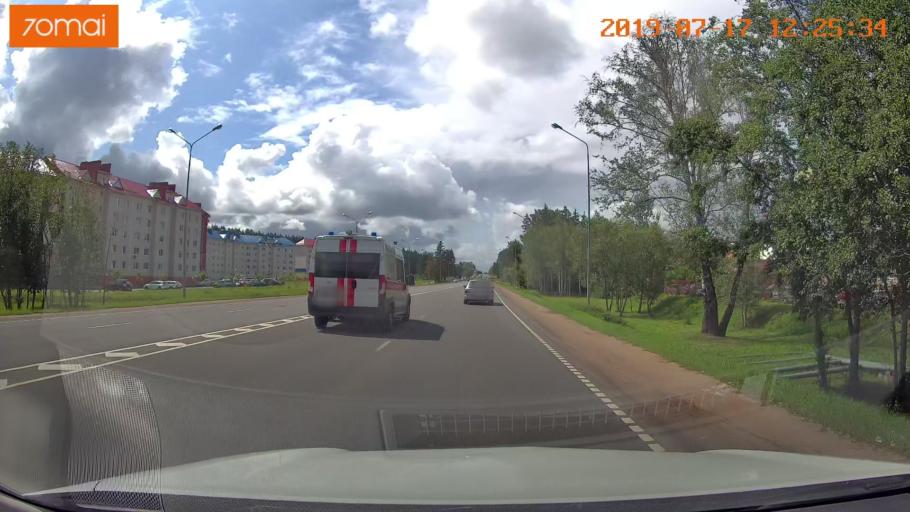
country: BY
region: Minsk
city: Borovlyany
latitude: 53.9909
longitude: 27.6681
